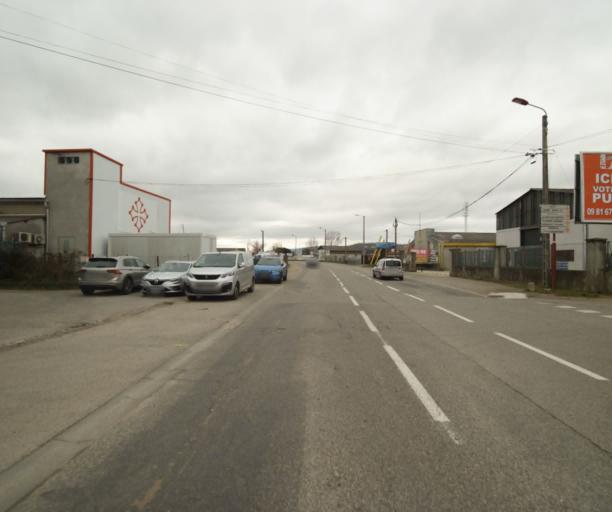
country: FR
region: Midi-Pyrenees
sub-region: Departement de l'Ariege
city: Pamiers
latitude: 43.1264
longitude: 1.6211
